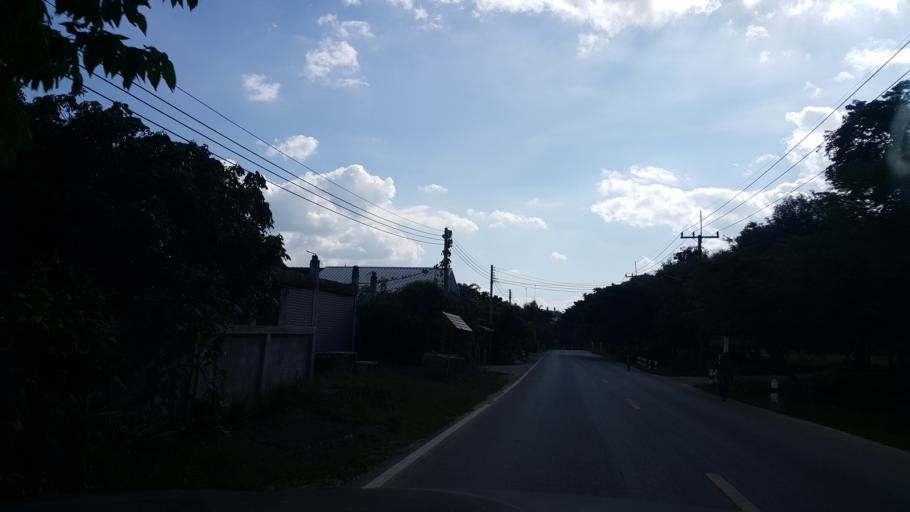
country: TH
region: Lamphun
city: Ban Thi
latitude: 18.5804
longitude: 99.2611
